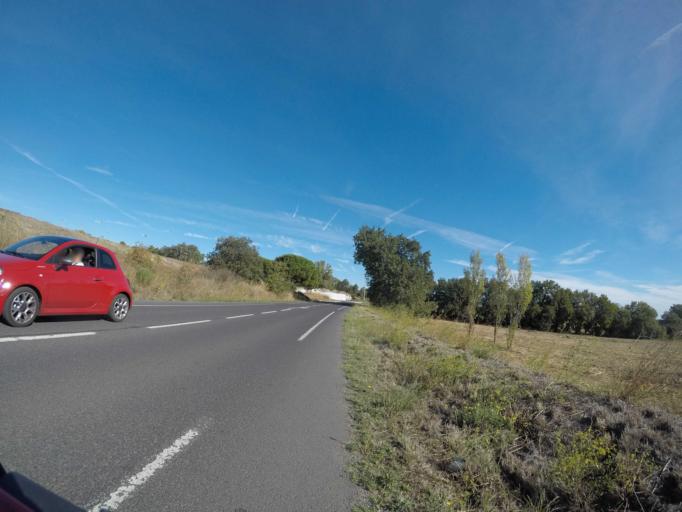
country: FR
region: Languedoc-Roussillon
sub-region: Departement des Pyrenees-Orientales
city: Ponteilla
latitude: 42.6224
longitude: 2.8118
